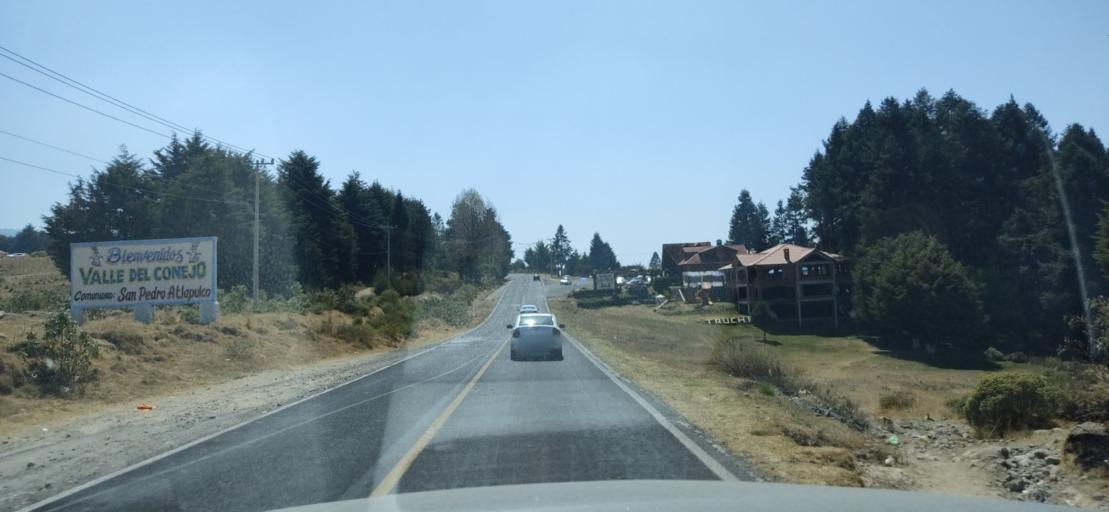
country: MX
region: Mexico
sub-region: Ocoyoacac
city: San Jeronimo Acazulco
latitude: 19.2673
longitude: -99.3764
